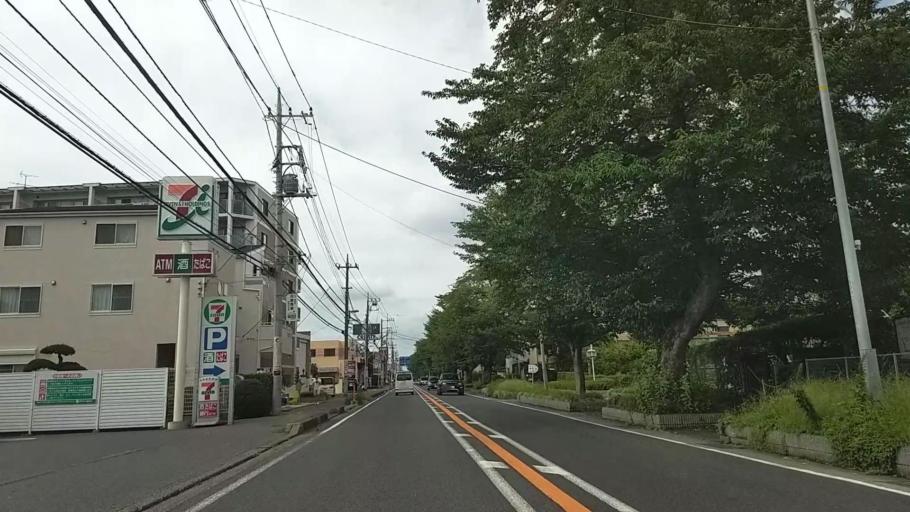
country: JP
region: Kanagawa
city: Minami-rinkan
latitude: 35.4445
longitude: 139.4673
